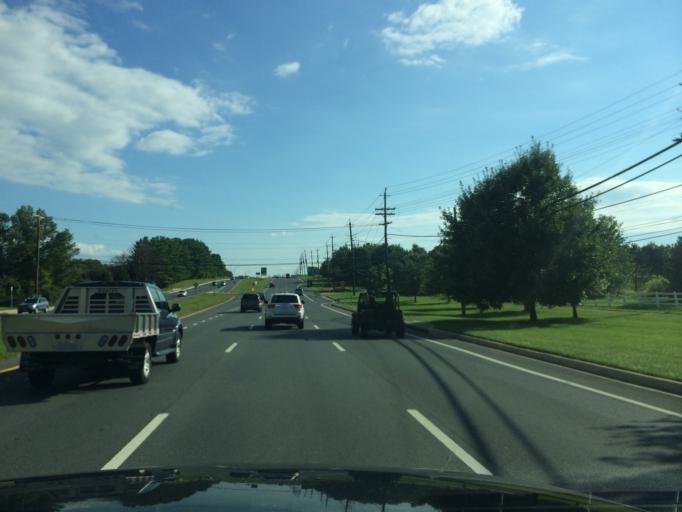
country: US
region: Maryland
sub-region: Montgomery County
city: Rossmoor
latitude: 39.1254
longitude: -77.0728
